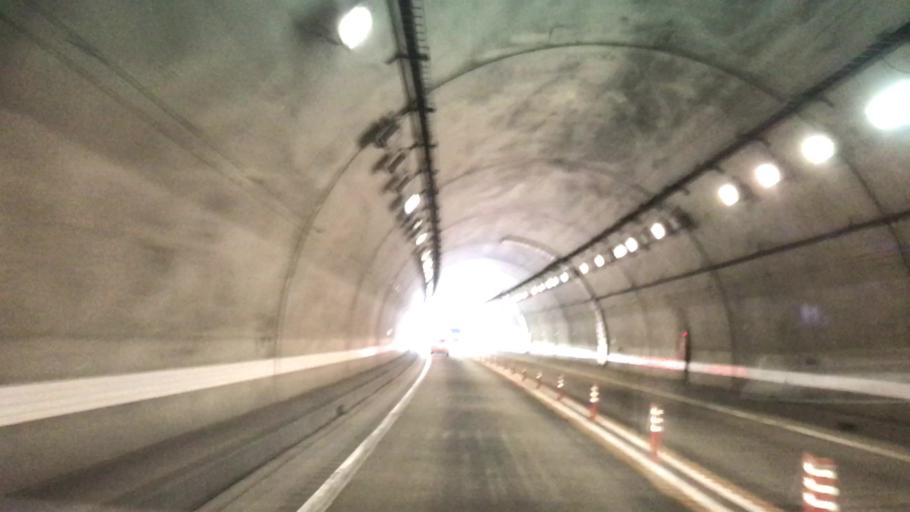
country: JP
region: Hokkaido
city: Shimo-furano
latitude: 42.9730
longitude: 142.3953
